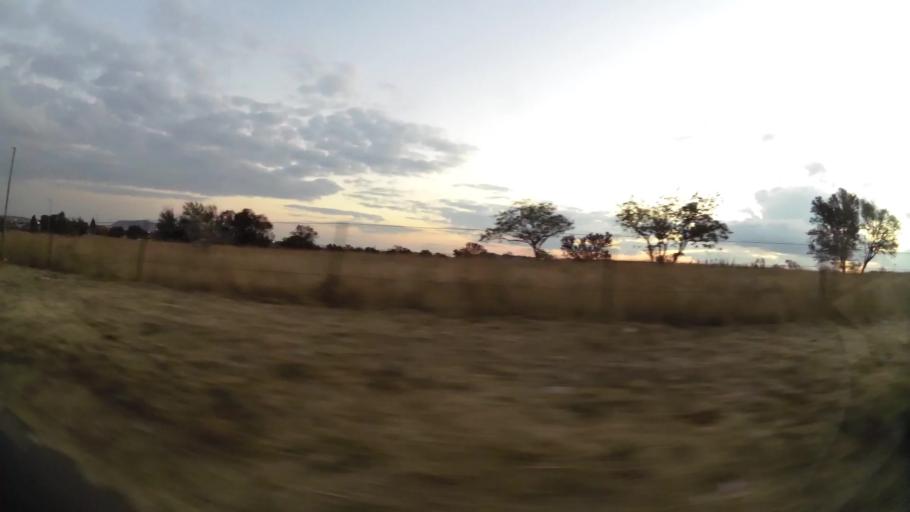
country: ZA
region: Orange Free State
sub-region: Mangaung Metropolitan Municipality
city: Bloemfontein
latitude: -29.1616
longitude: 26.1957
